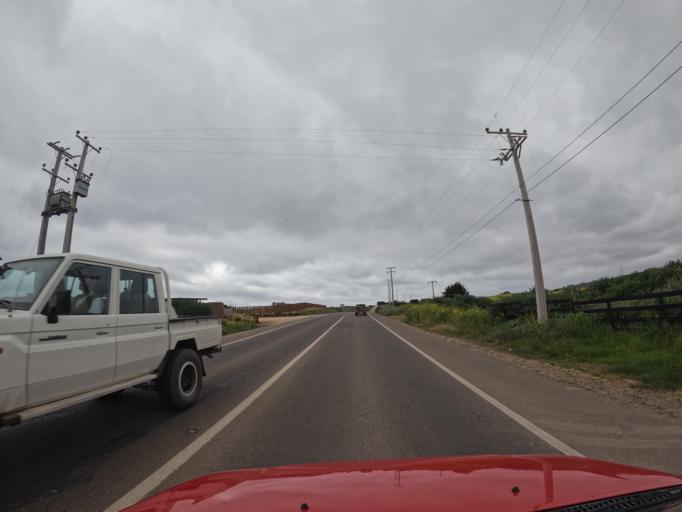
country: CL
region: O'Higgins
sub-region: Provincia de Colchagua
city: Santa Cruz
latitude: -34.4483
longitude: -72.0312
